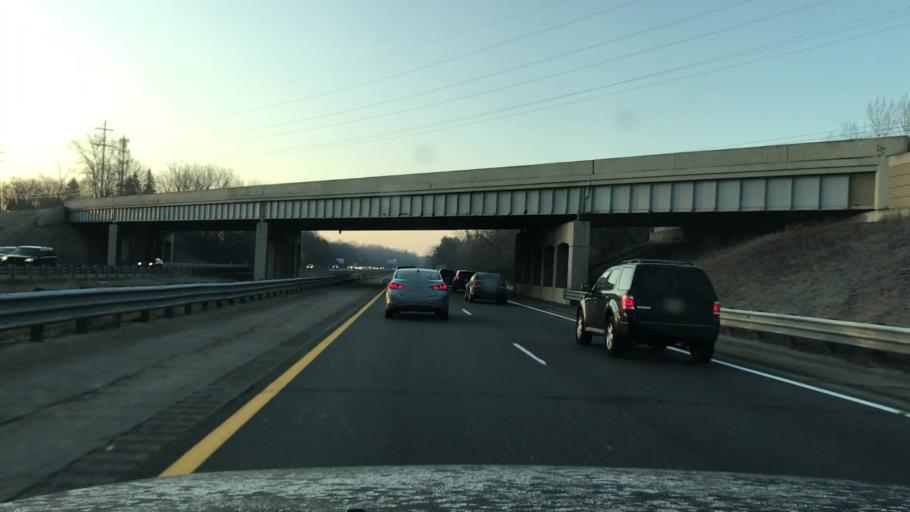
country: US
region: Michigan
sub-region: Kent County
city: East Grand Rapids
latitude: 42.9624
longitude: -85.5786
